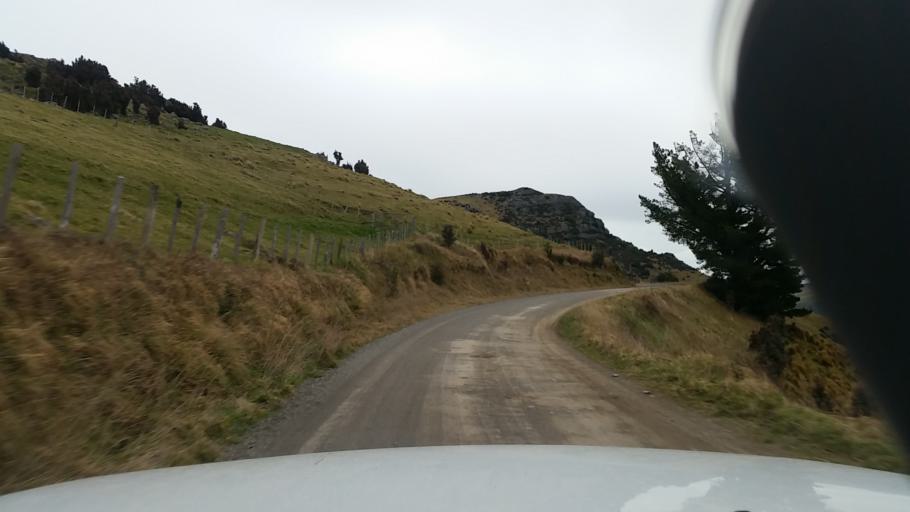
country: NZ
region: Canterbury
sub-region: Christchurch City
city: Christchurch
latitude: -43.8160
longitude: 172.7952
